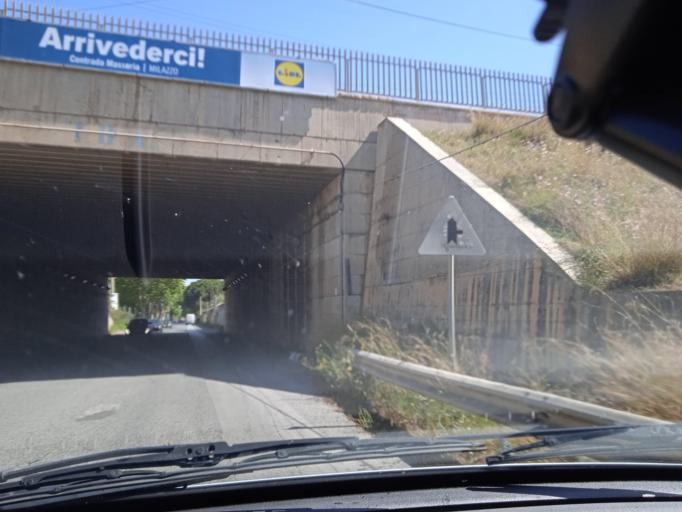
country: IT
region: Sicily
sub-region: Messina
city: Milazzo
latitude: 38.1981
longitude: 15.2526
